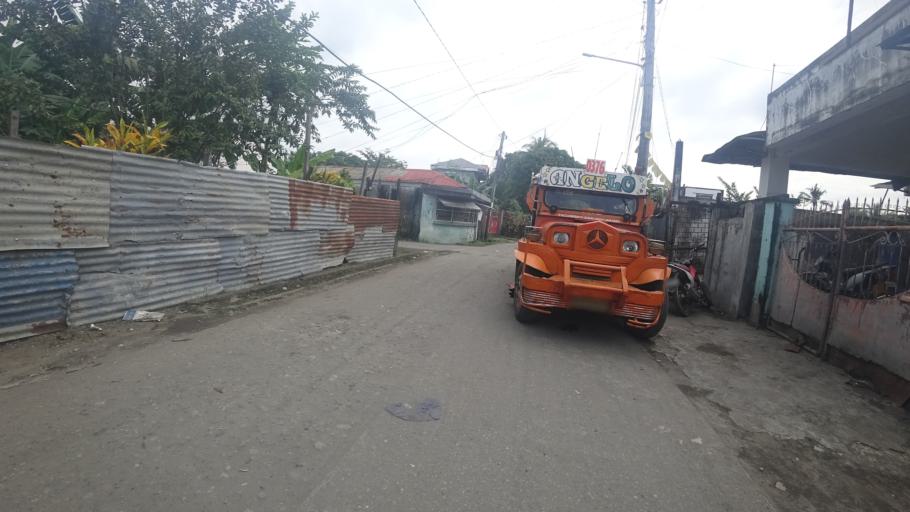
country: PH
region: Eastern Visayas
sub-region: Province of Leyte
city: Baras
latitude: 11.2057
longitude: 125.0116
